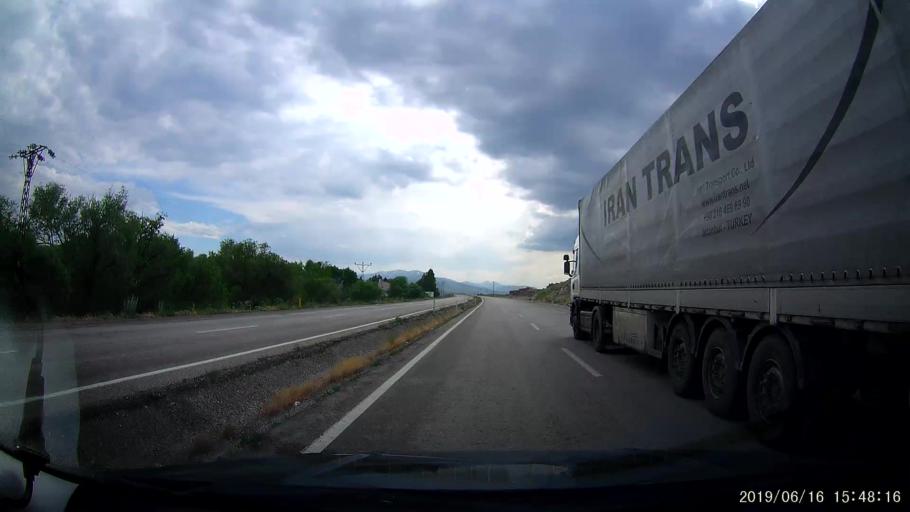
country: TR
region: Erzurum
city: Pasinler
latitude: 39.9843
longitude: 41.7049
